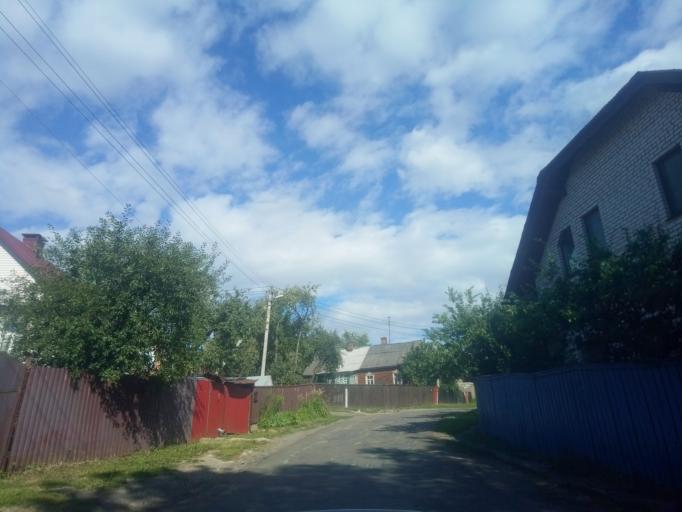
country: BY
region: Minsk
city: Minsk
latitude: 53.8881
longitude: 27.5091
